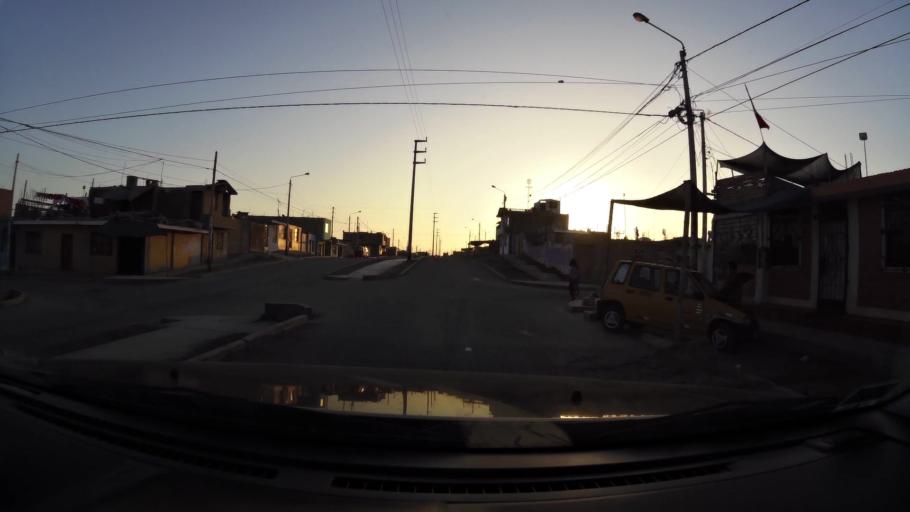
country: PE
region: Ica
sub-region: Provincia de Pisco
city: San Clemente
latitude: -13.6782
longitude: -76.1535
